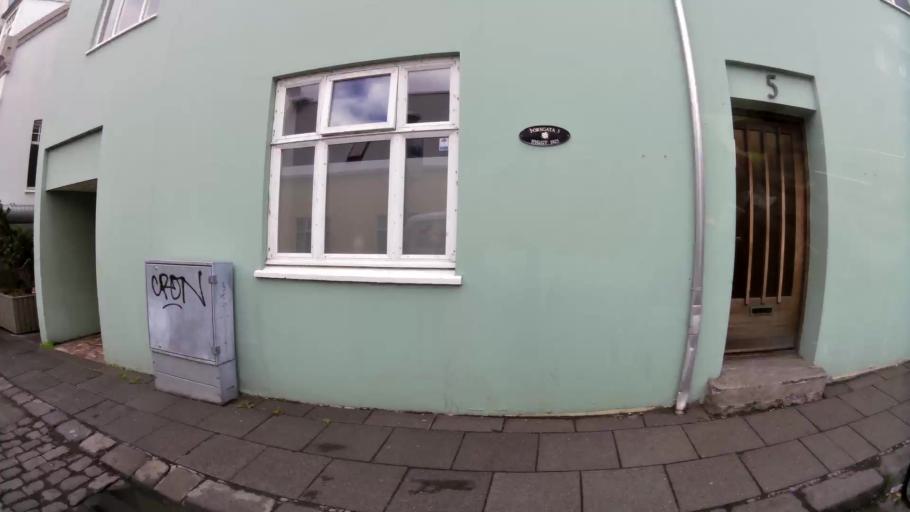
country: IS
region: Capital Region
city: Kopavogur
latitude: 64.1437
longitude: -21.9314
